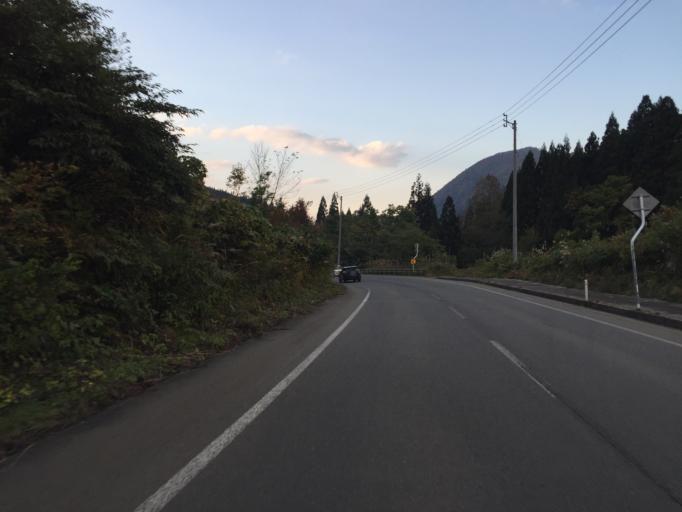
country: JP
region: Yamagata
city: Yonezawa
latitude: 37.8411
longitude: 140.0000
